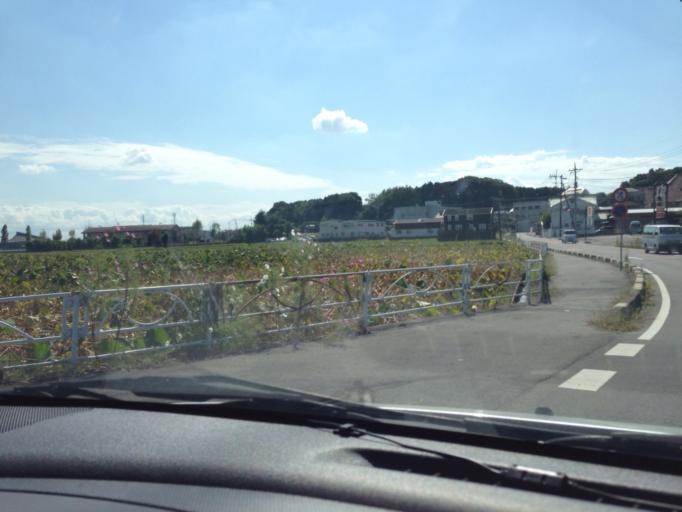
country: JP
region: Ibaraki
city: Ami
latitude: 36.0679
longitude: 140.2107
